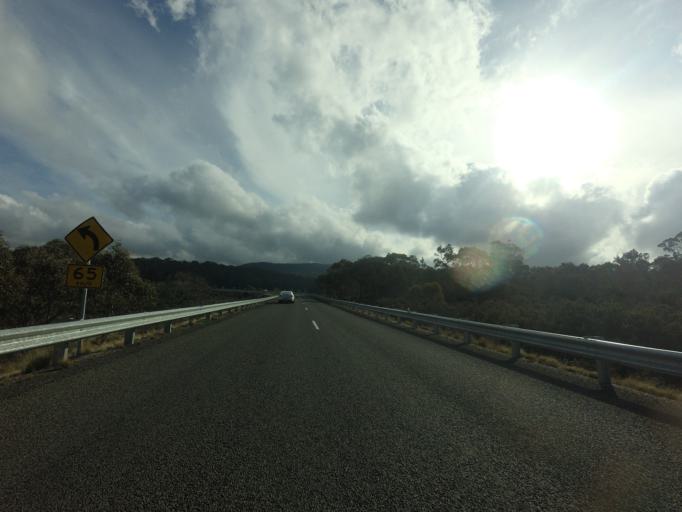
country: AU
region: Tasmania
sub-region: Meander Valley
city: Deloraine
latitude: -41.7864
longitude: 146.6961
